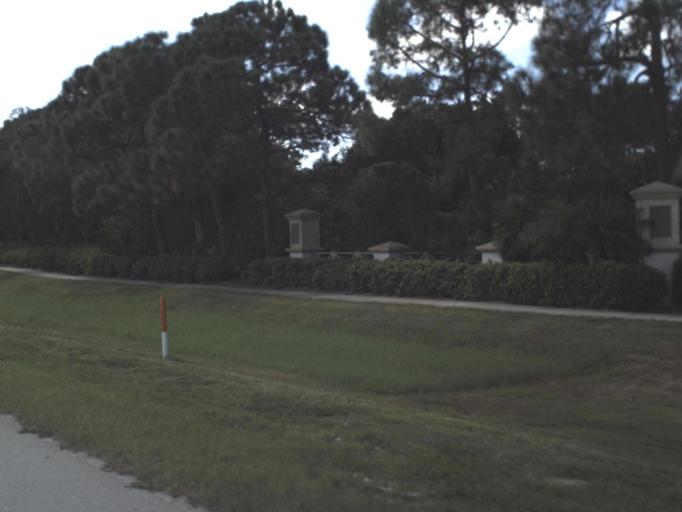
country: US
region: Florida
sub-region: Lee County
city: Bonita Springs
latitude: 26.3635
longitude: -81.8079
